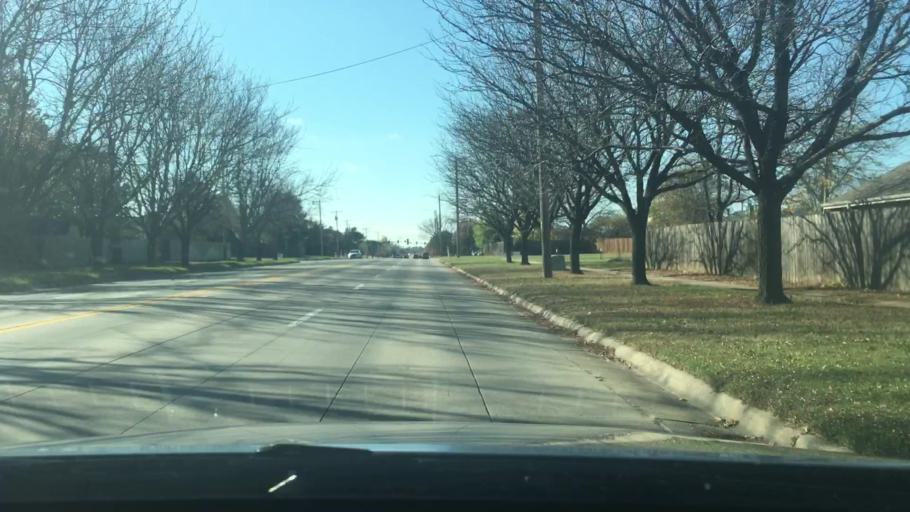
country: US
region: Kansas
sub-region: Sedgwick County
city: Maize
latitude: 37.6936
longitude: -97.4768
